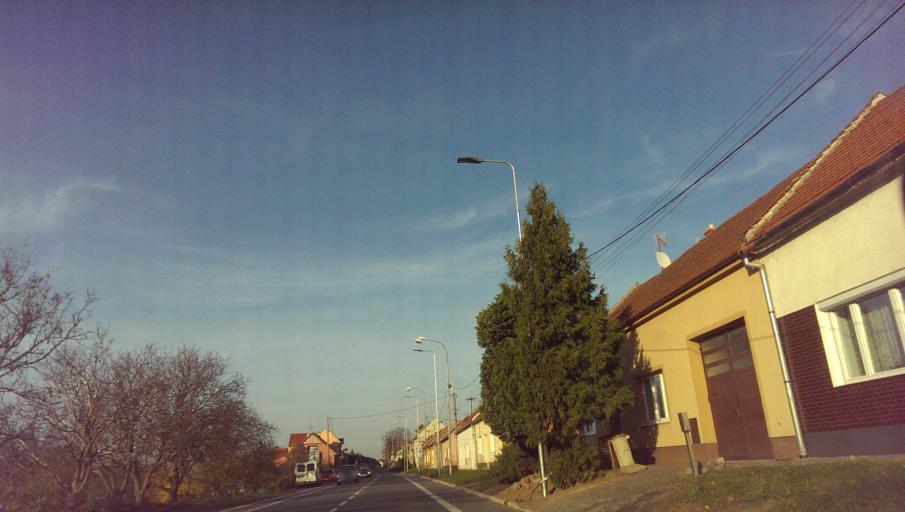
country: CZ
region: Zlin
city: Kunovice
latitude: 49.0345
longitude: 17.4607
